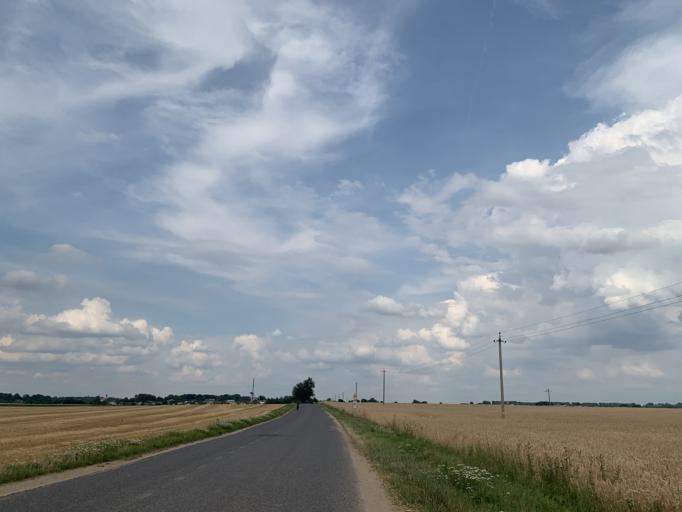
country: BY
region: Minsk
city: Nyasvizh
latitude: 53.2007
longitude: 26.6737
